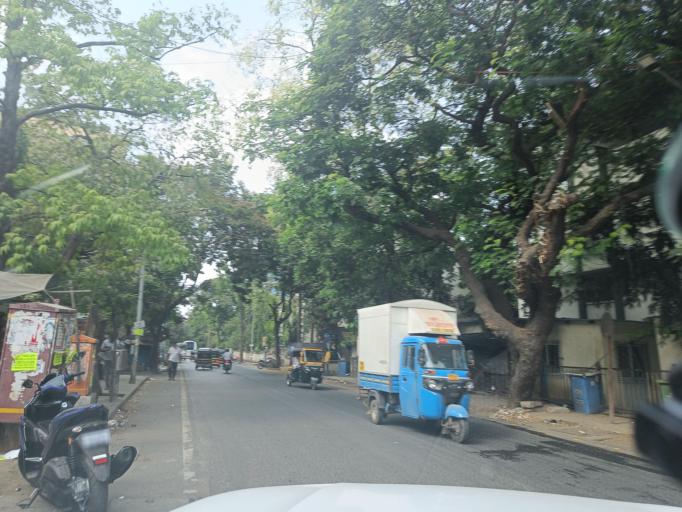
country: IN
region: Maharashtra
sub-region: Mumbai Suburban
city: Powai
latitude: 19.1179
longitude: 72.8685
